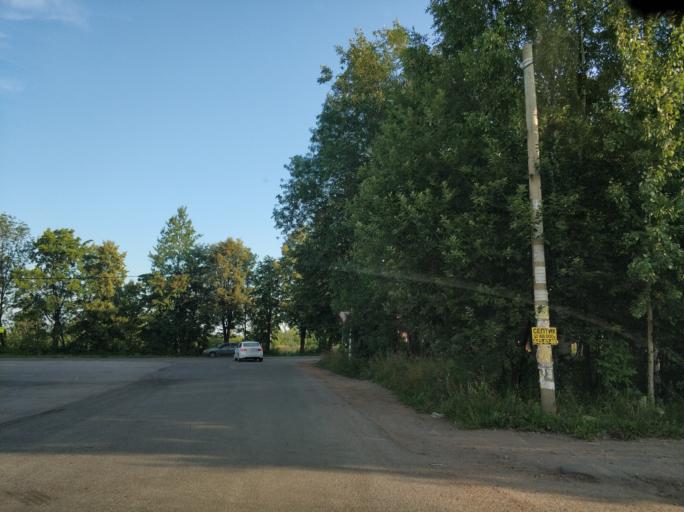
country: RU
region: Leningrad
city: Romanovka
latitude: 60.0553
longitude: 30.7402
